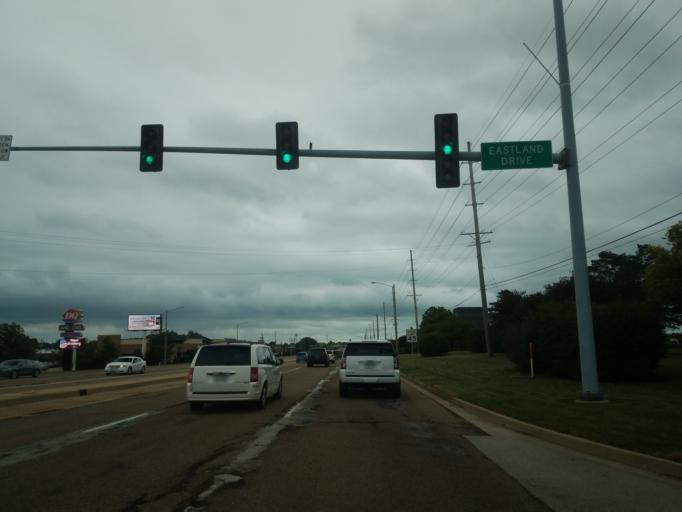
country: US
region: Illinois
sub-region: McLean County
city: Bloomington
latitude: 40.4838
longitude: -88.9529
